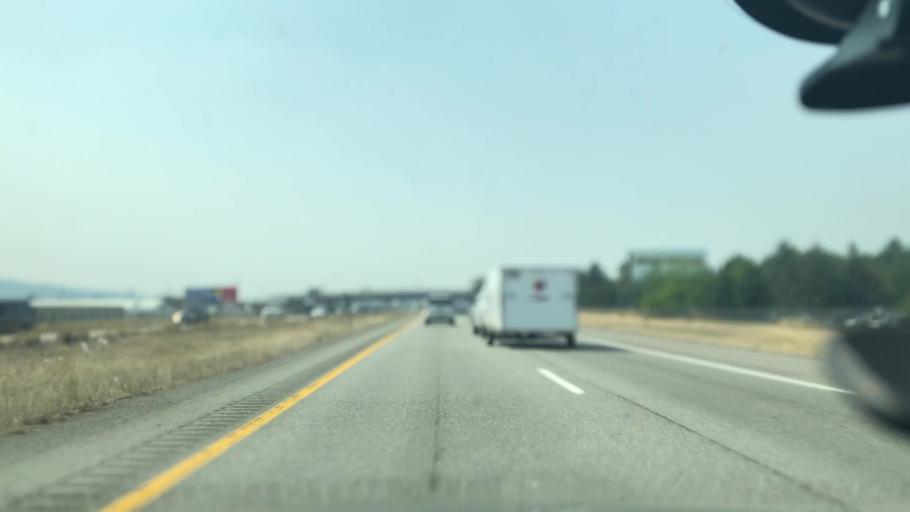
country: US
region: Idaho
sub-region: Kootenai County
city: Post Falls
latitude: 47.7126
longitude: -116.9104
